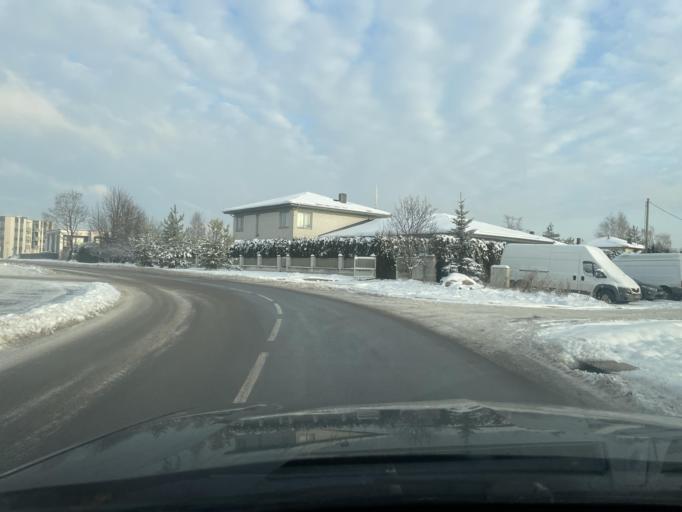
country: EE
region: Tartu
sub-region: Tartu linn
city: Tartu
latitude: 58.3542
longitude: 26.6898
